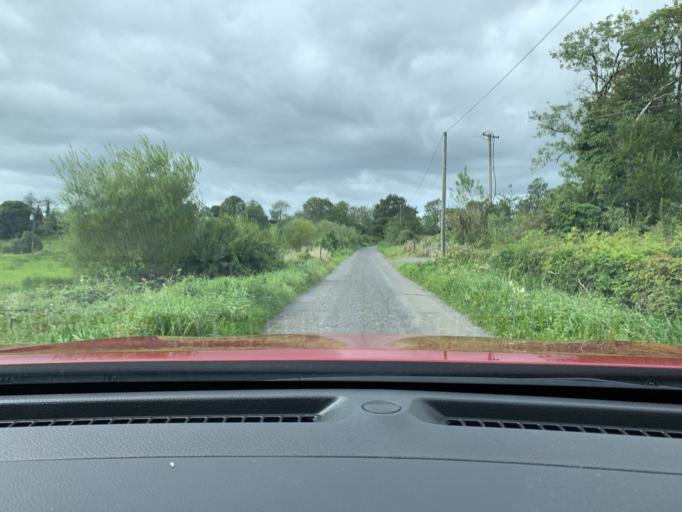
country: IE
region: Connaught
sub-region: Sligo
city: Collooney
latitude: 54.1583
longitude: -8.4293
